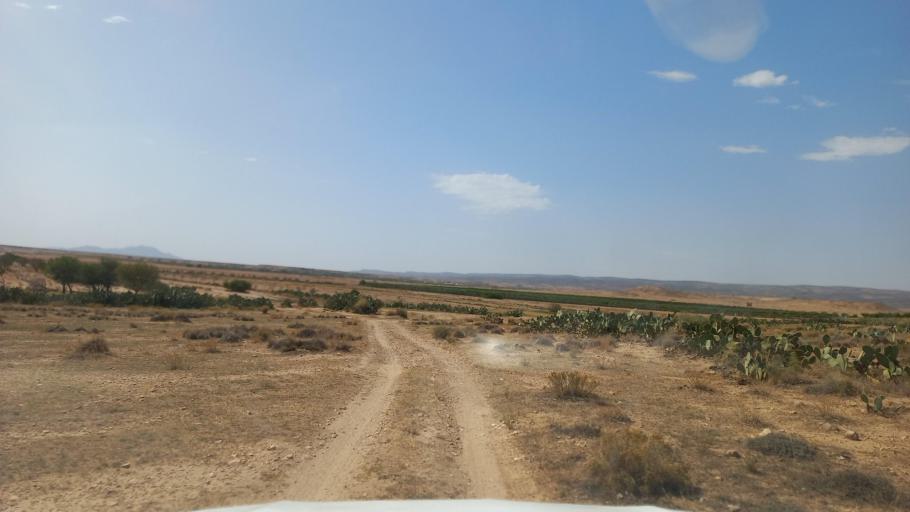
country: TN
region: Al Qasrayn
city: Kasserine
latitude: 35.2589
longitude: 8.9728
